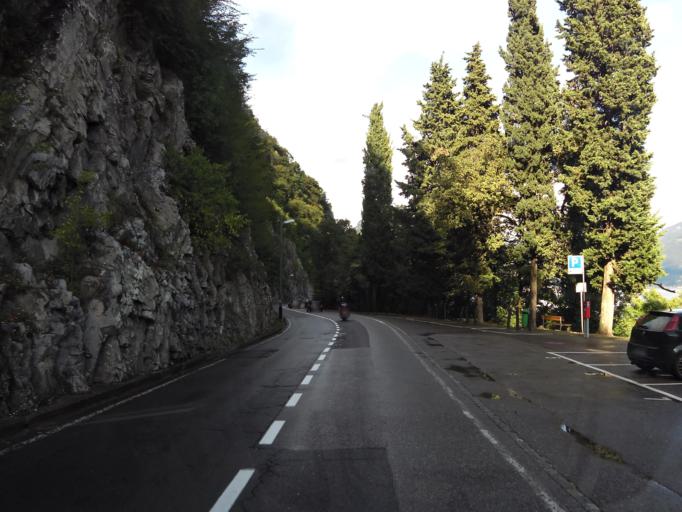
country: IT
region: Lombardy
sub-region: Provincia di Como
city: Lanzo d'Intelvi
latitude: 46.0121
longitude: 9.0134
